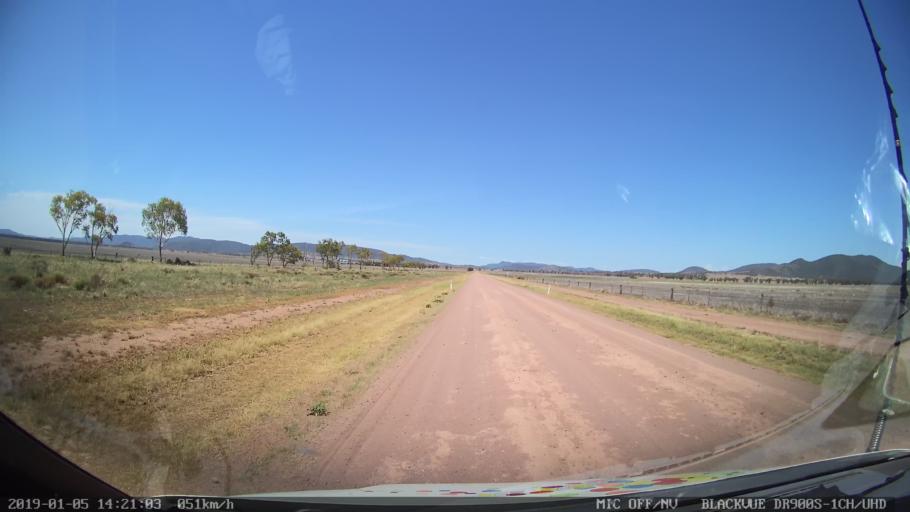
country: AU
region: New South Wales
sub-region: Liverpool Plains
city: Quirindi
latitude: -31.2472
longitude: 150.5100
